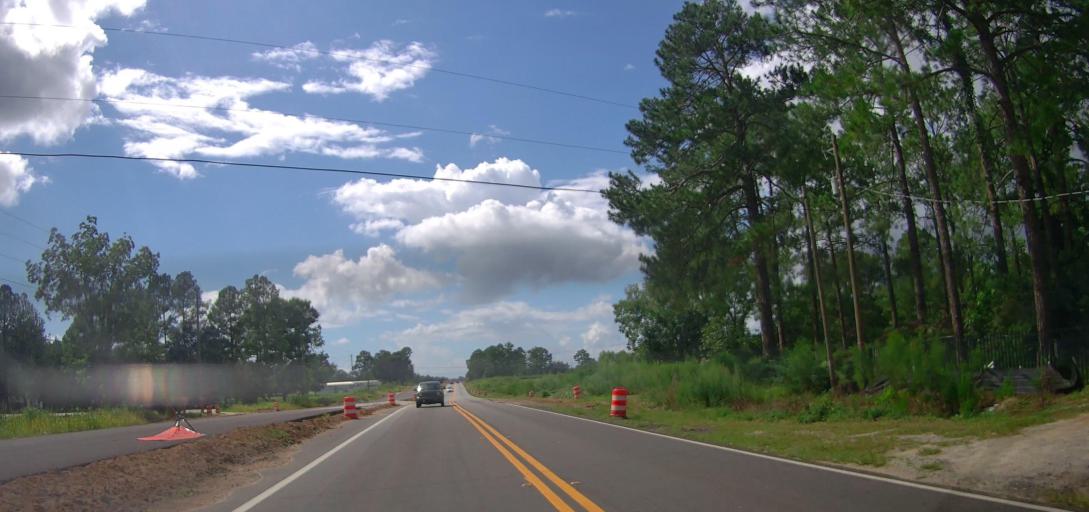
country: US
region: Georgia
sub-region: Coffee County
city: Douglas
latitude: 31.5284
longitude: -82.9076
